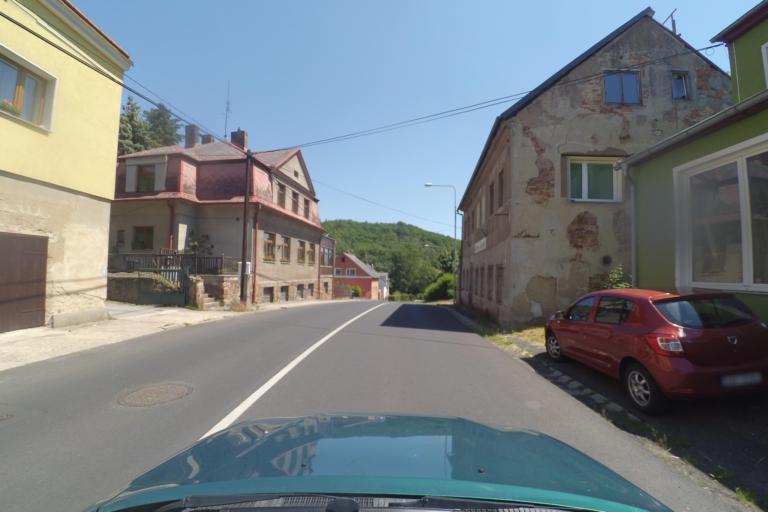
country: CZ
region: Ustecky
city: Dubi
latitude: 50.6799
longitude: 13.8075
